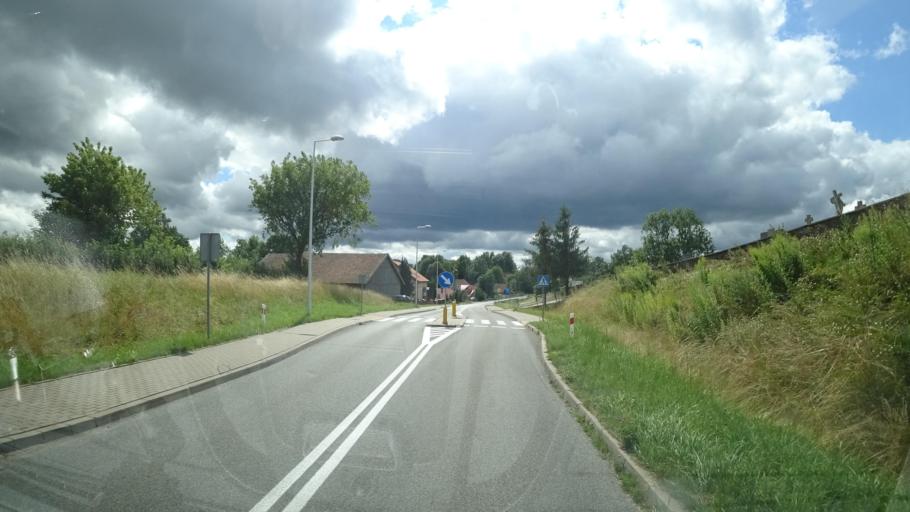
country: PL
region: Warmian-Masurian Voivodeship
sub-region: Powiat goldapski
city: Goldap
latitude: 54.2285
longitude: 22.2445
